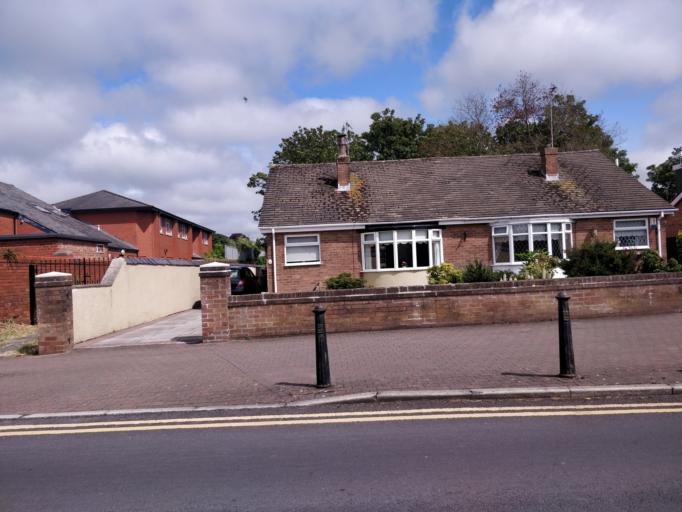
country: GB
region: England
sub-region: Sefton
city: Southport
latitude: 53.6610
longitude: -2.9628
